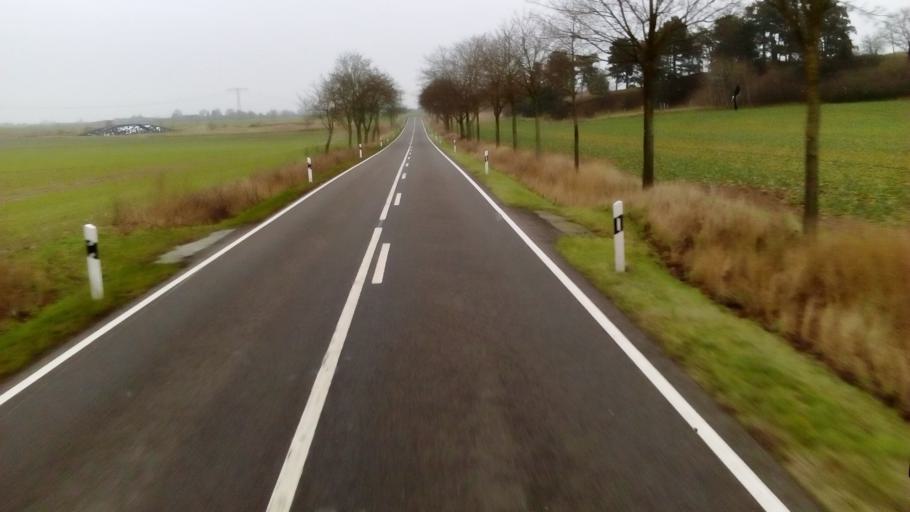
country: DE
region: Brandenburg
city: Goritz
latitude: 53.4939
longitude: 13.8885
